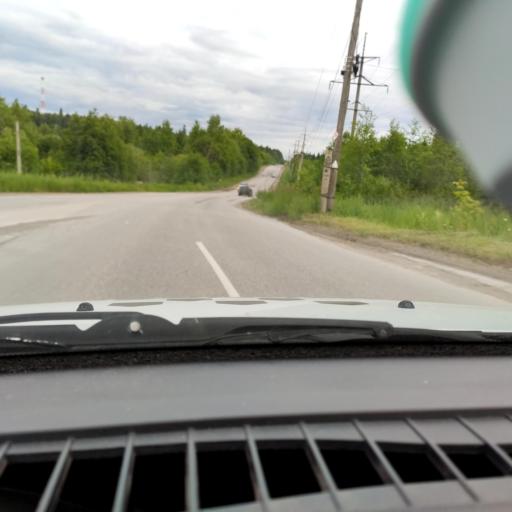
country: RU
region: Perm
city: Chusovoy
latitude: 58.2623
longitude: 57.8265
